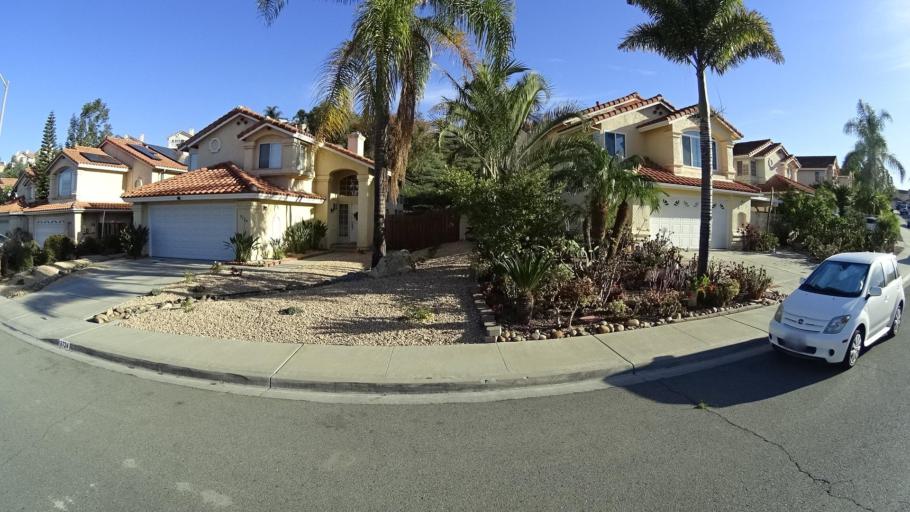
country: US
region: California
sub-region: San Diego County
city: La Presa
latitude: 32.7121
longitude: -116.9878
